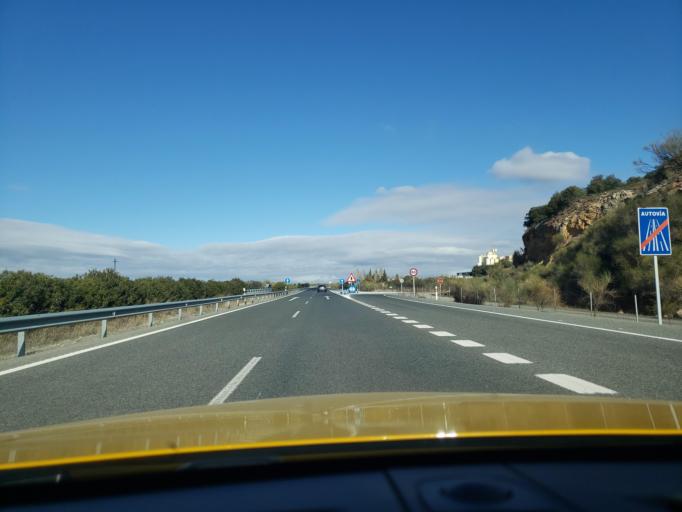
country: ES
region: Andalusia
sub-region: Provincia de Malaga
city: Villanueva del Trabuco
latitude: 37.0926
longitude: -4.3155
